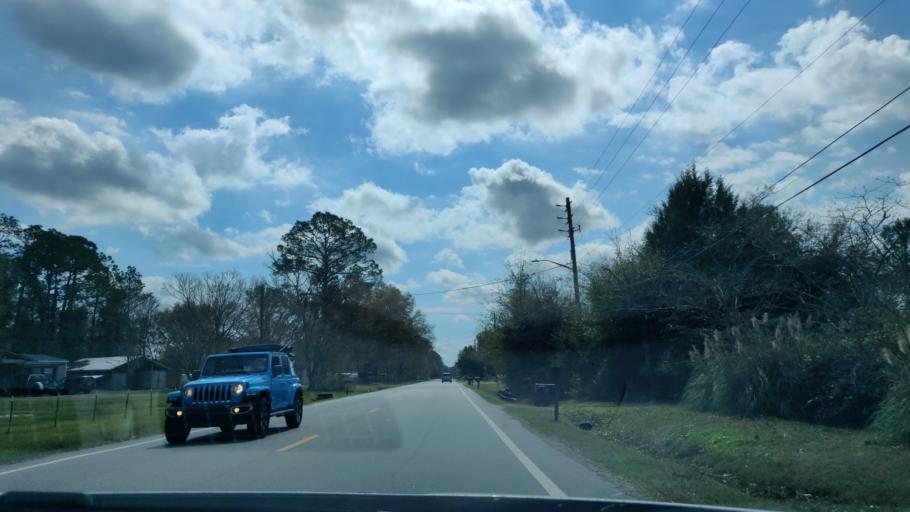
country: US
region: Florida
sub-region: Duval County
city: Baldwin
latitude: 30.3309
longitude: -81.9001
